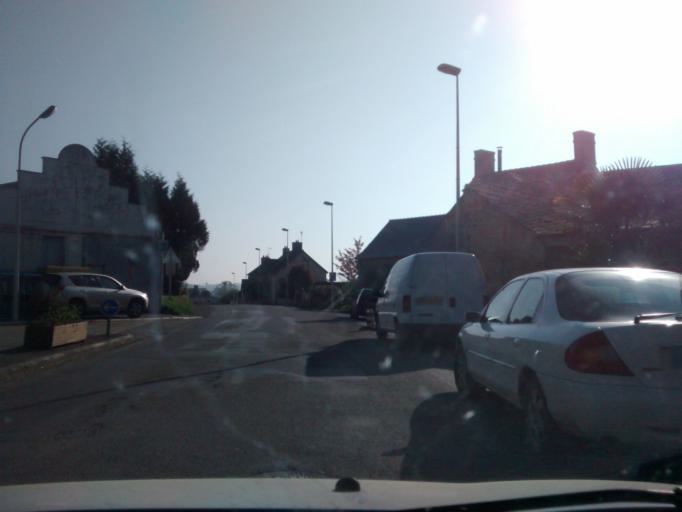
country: FR
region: Brittany
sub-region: Departement d'Ille-et-Vilaine
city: Romagne
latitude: 48.2732
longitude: -1.2932
